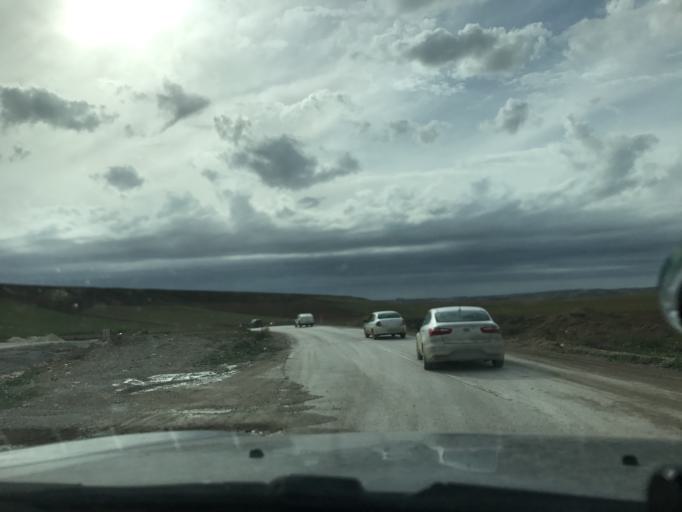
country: TN
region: Silyanah
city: Siliana
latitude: 36.1193
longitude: 9.5926
